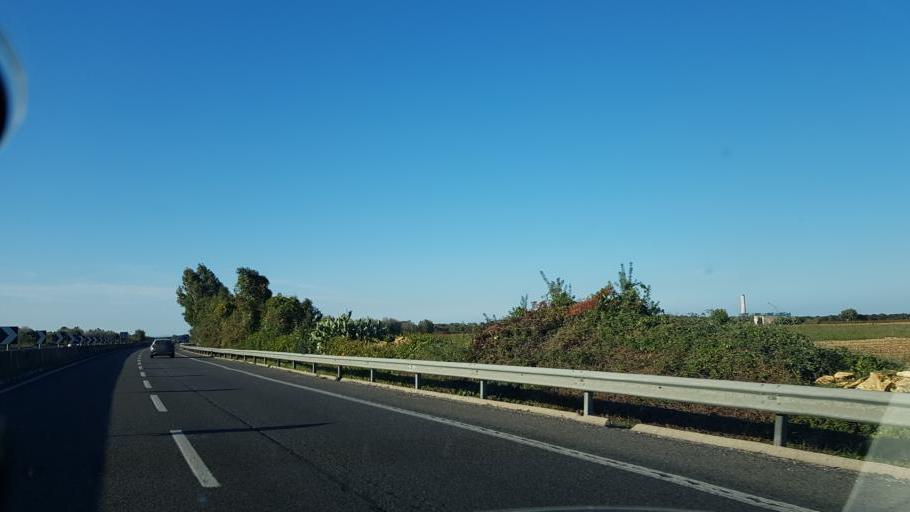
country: IT
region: Apulia
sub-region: Provincia di Brindisi
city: San Pietro Vernotico
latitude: 40.5232
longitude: 18.0152
